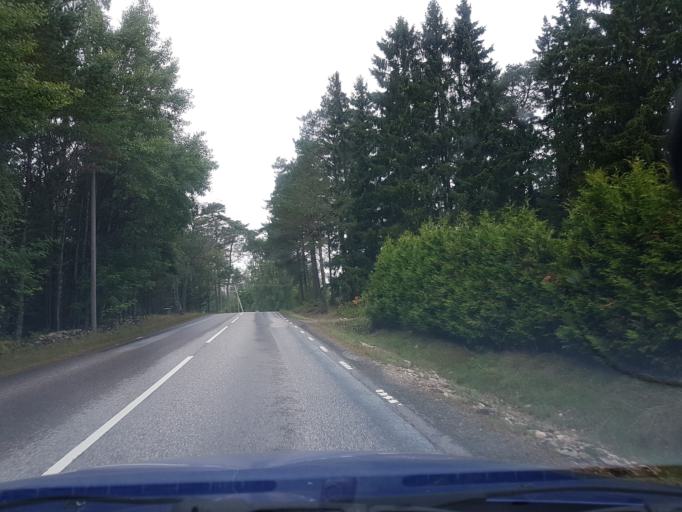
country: SE
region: Vaestra Goetaland
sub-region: Ale Kommun
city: Salanda
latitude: 57.9230
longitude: 12.2753
